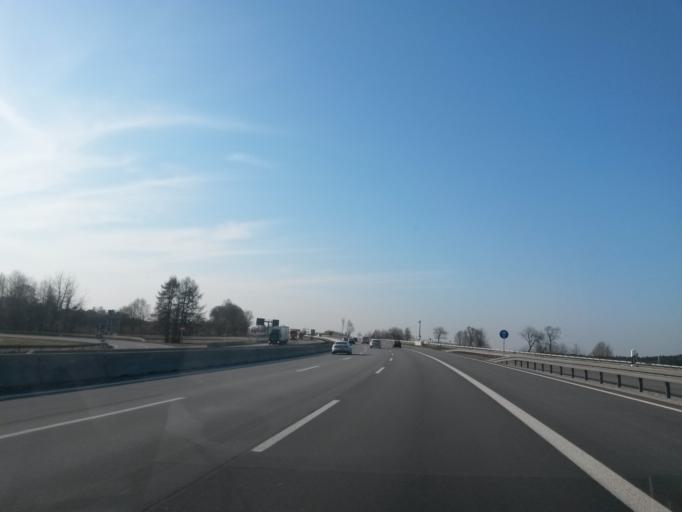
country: DE
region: Bavaria
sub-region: Upper Bavaria
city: Wolnzach
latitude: 48.5801
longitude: 11.5904
